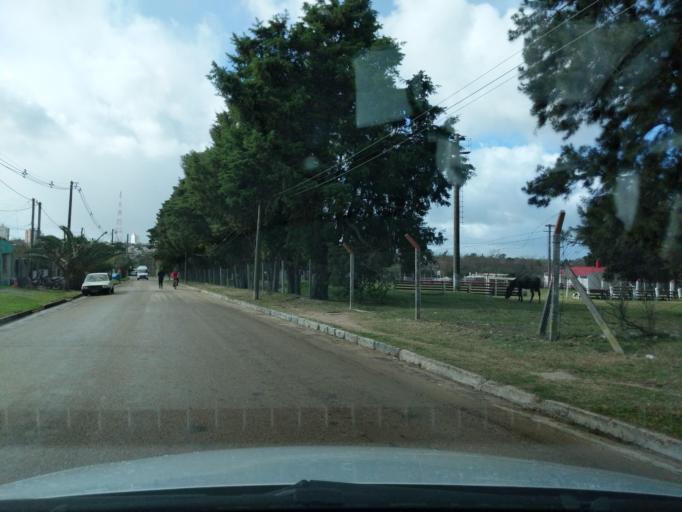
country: UY
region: Florida
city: Florida
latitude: -34.1041
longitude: -56.2260
